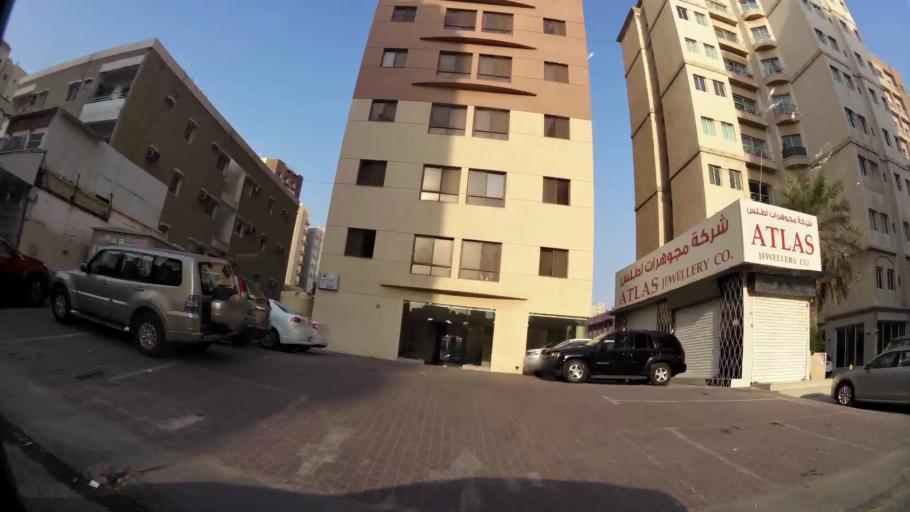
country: KW
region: Muhafazat Hawalli
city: As Salimiyah
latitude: 29.3291
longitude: 48.0616
